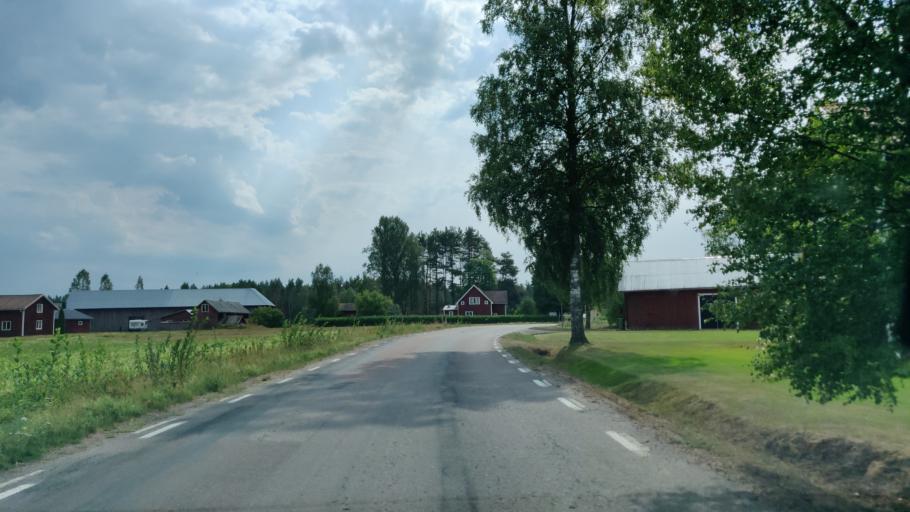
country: SE
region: Vaermland
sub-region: Munkfors Kommun
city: Munkfors
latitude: 59.8950
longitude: 13.5276
